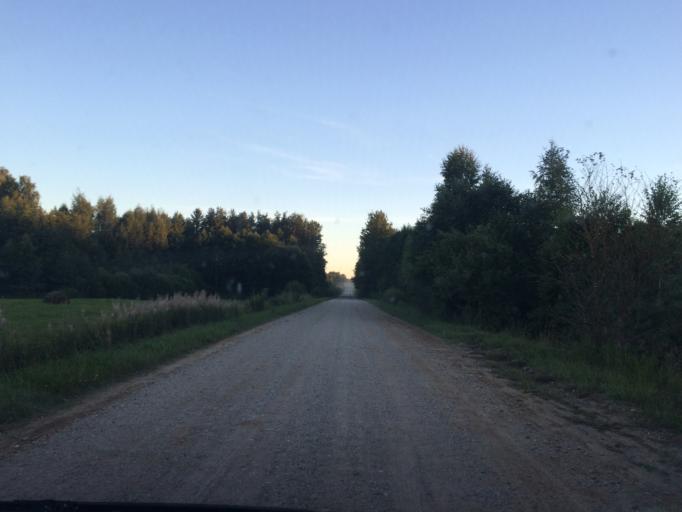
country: LV
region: Aglona
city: Aglona
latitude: 56.1827
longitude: 27.2146
